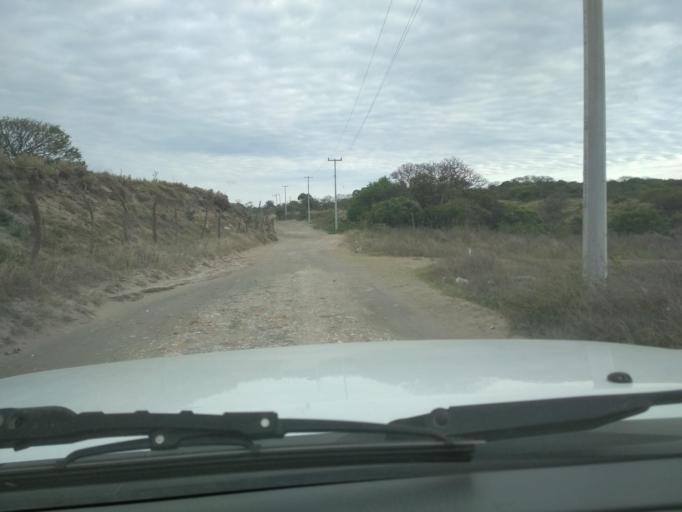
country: MX
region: Veracruz
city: Anton Lizardo
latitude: 19.0516
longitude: -95.9929
